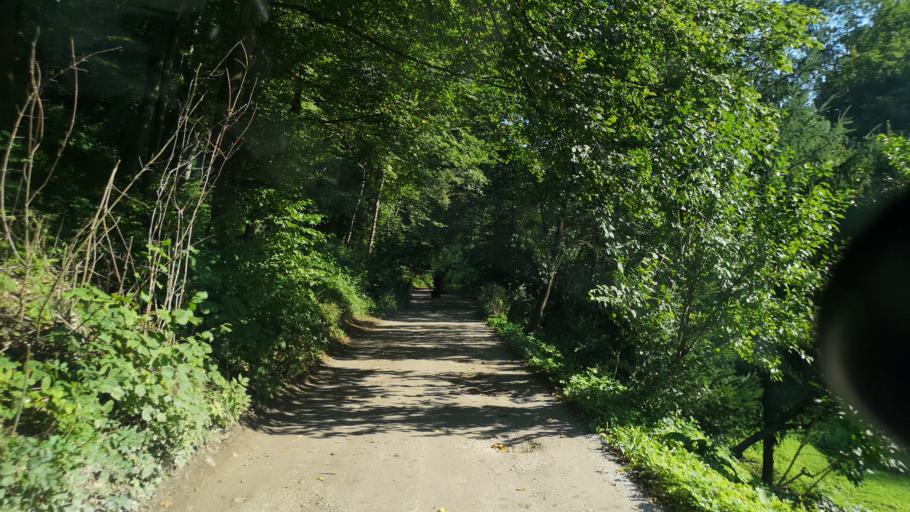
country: SK
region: Trnavsky
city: Smolenice
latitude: 48.5581
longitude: 17.4276
